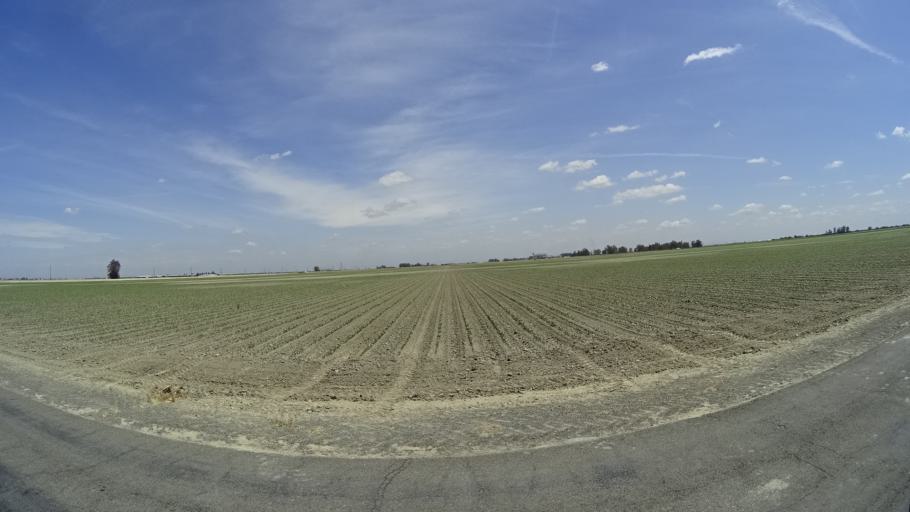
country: US
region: California
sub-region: Kings County
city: Home Garden
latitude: 36.2226
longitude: -119.6728
